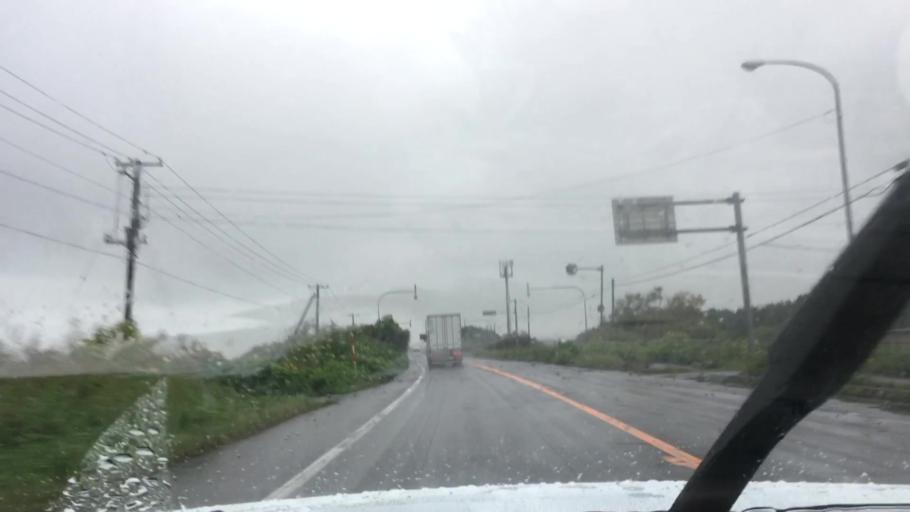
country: JP
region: Hokkaido
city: Niseko Town
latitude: 42.4329
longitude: 140.3193
